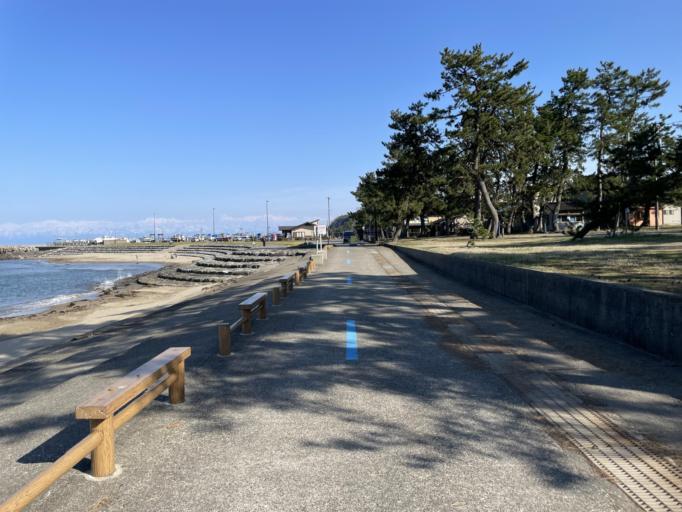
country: JP
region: Toyama
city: Himi
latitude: 36.8220
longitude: 137.0280
